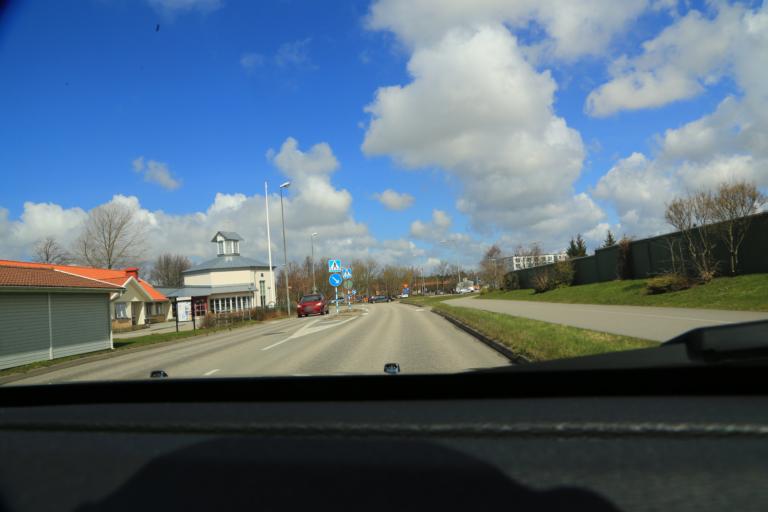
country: SE
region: Halland
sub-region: Varbergs Kommun
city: Varberg
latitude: 57.1104
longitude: 12.2754
